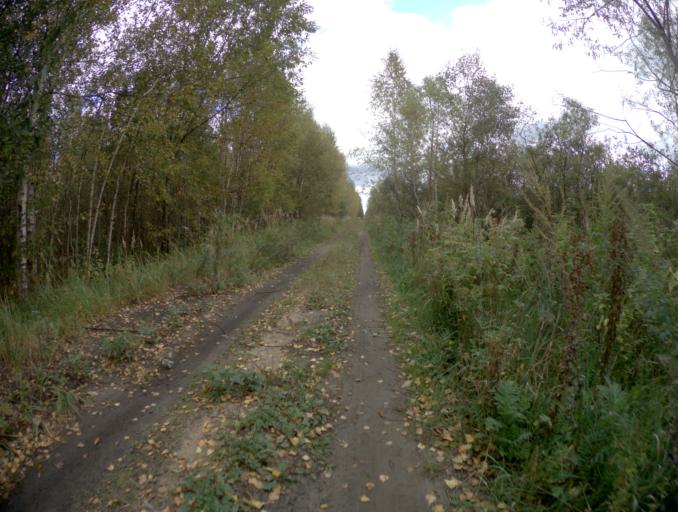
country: RU
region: Vladimir
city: Urshel'skiy
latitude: 55.7468
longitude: 40.0853
